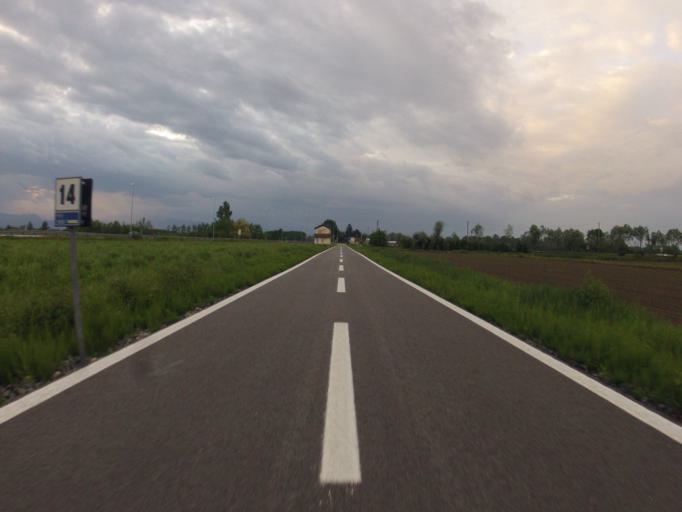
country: IT
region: Piedmont
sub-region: Provincia di Torino
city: Villafranca Piemonte
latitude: 44.8041
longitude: 7.5030
